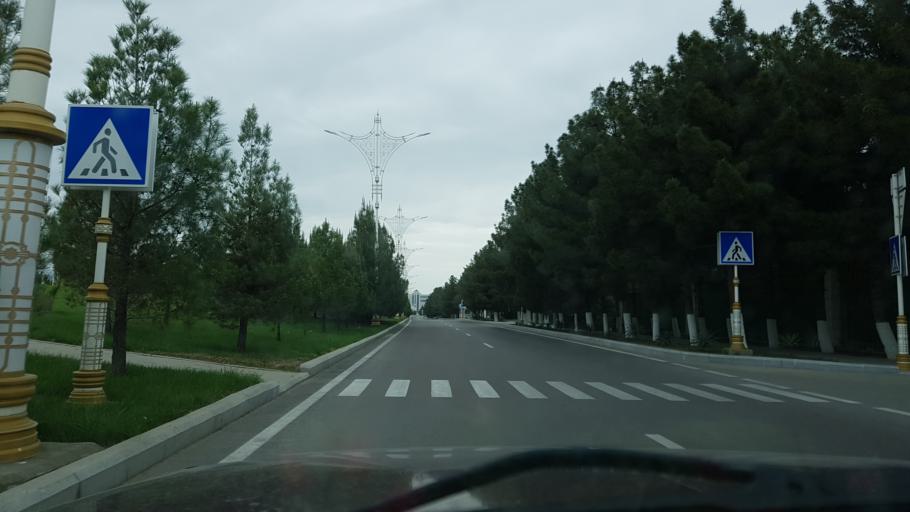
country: TM
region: Ahal
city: Ashgabat
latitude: 37.8860
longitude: 58.3566
